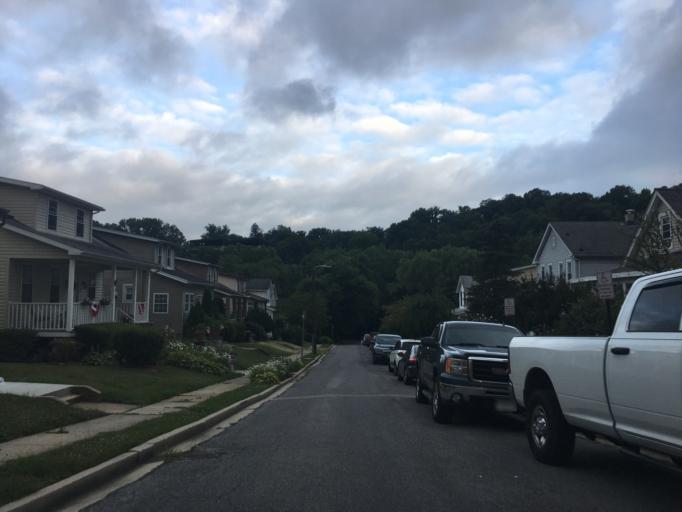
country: US
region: Maryland
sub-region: Baltimore County
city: Lutherville
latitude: 39.3723
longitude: -76.6502
